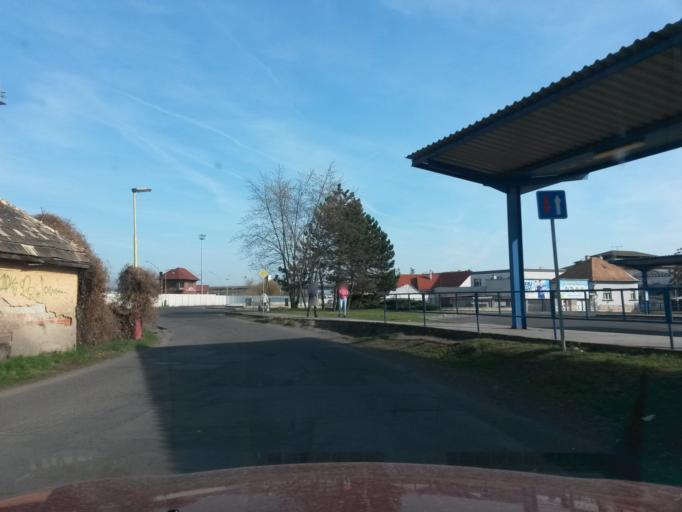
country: SK
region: Banskobystricky
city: Lucenec
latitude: 48.3345
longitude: 19.6689
